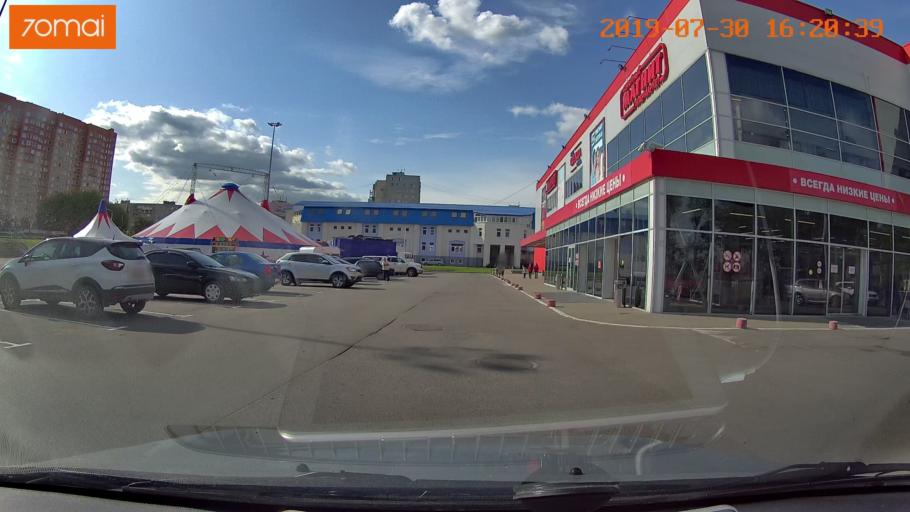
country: RU
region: Moskovskaya
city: Voskresensk
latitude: 55.3122
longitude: 38.6567
